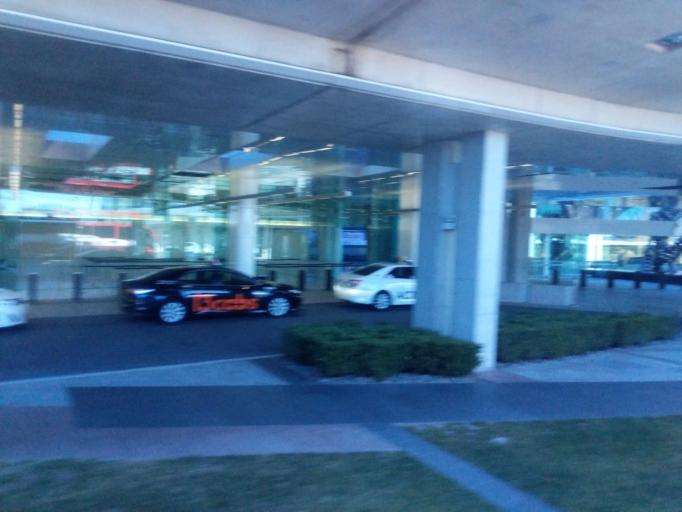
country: AU
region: Australian Capital Territory
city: Forrest
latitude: -35.3077
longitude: 149.1899
